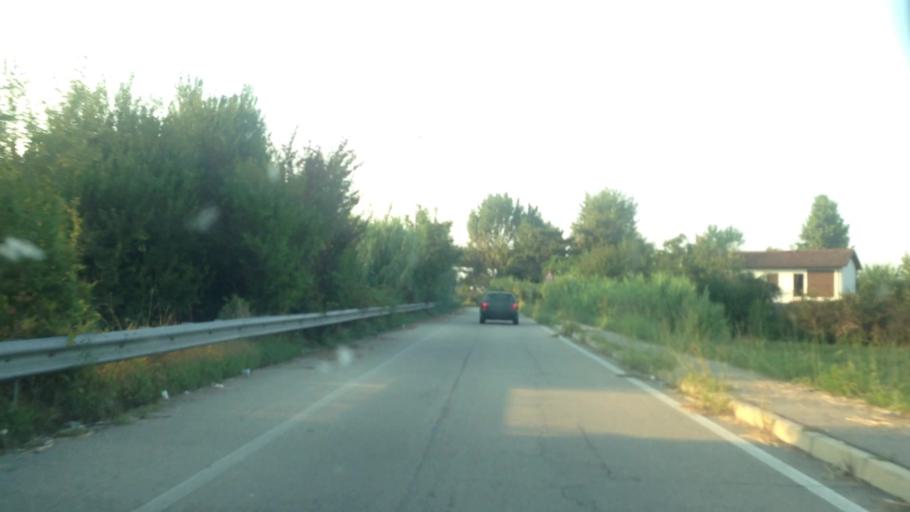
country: IT
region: Piedmont
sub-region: Provincia di Asti
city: Asti
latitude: 44.9151
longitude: 8.2286
